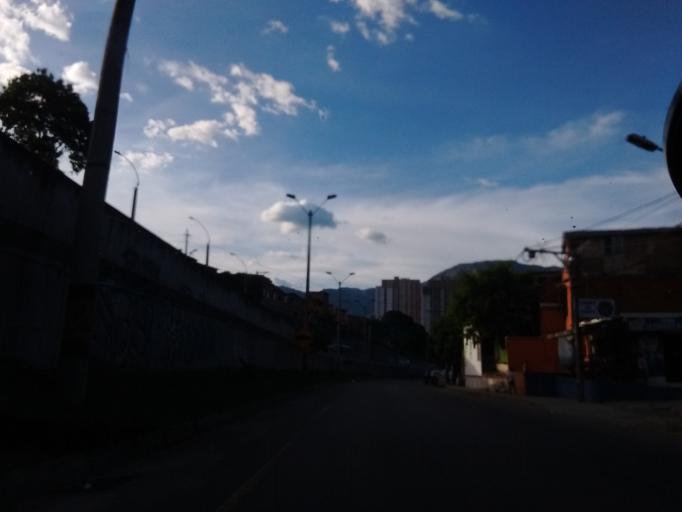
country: CO
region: Antioquia
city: Bello
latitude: 6.3076
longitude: -75.5583
